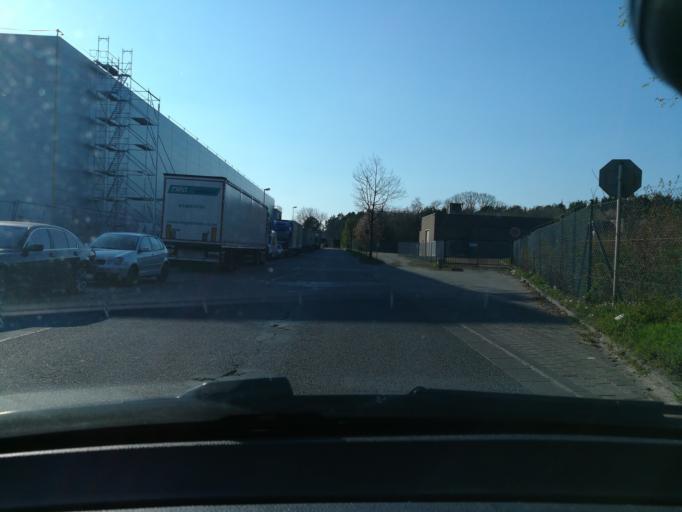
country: DE
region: North Rhine-Westphalia
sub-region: Regierungsbezirk Detmold
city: Verl
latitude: 51.9434
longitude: 8.5681
